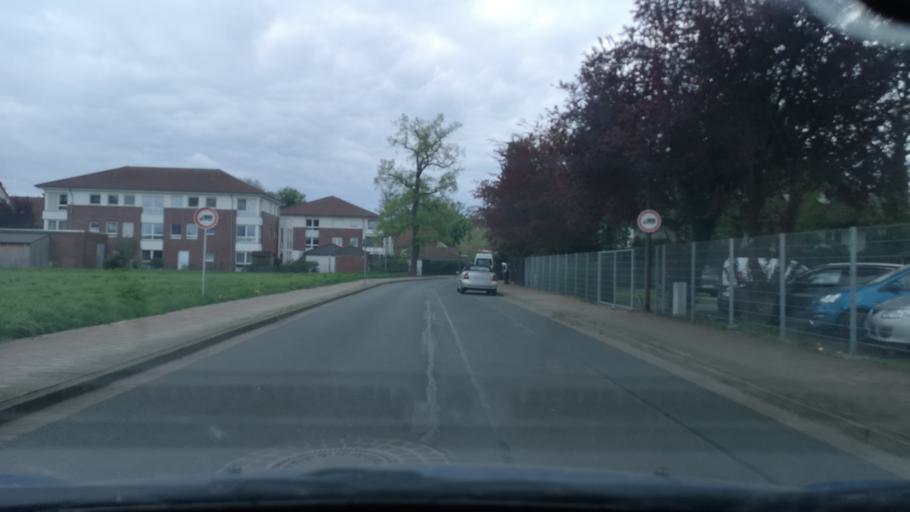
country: DE
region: Lower Saxony
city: Langenhagen
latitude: 52.4764
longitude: 9.7440
